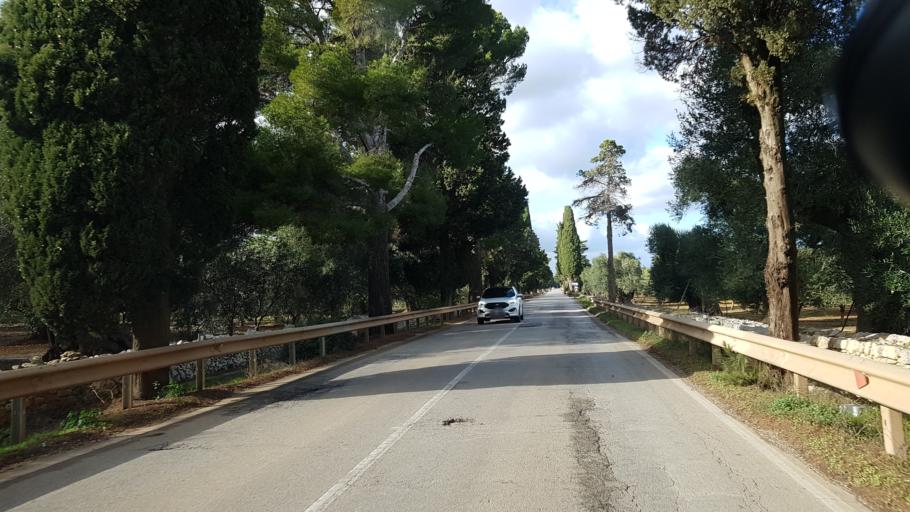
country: IT
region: Apulia
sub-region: Provincia di Brindisi
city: Montalbano
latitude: 40.7583
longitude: 17.5339
